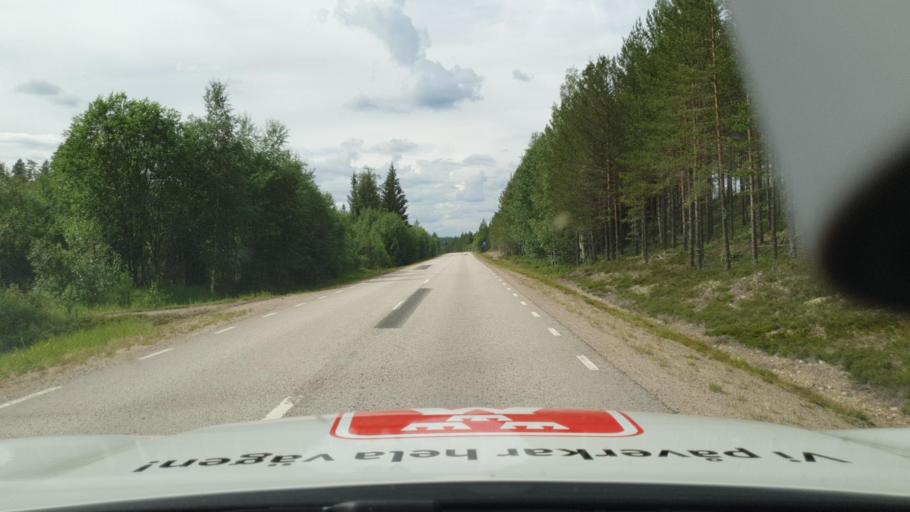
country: NO
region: Hedmark
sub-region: Trysil
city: Innbygda
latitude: 60.9210
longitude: 12.5323
